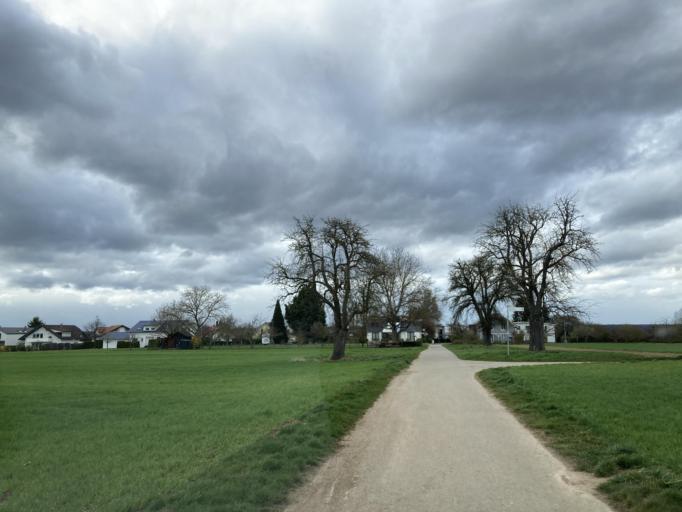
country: DE
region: Baden-Wuerttemberg
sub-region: Tuebingen Region
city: Wannweil
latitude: 48.5270
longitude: 9.1628
